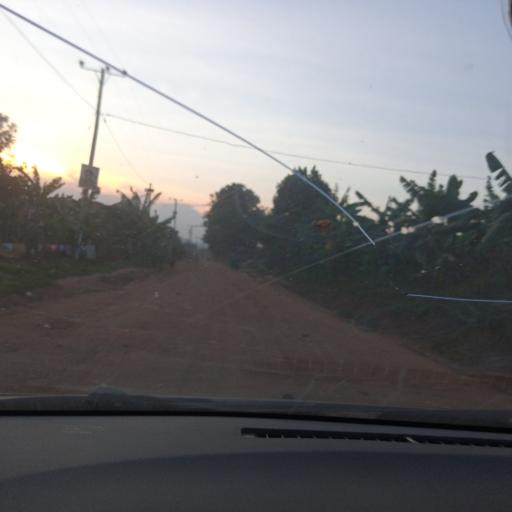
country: UG
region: Central Region
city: Masaka
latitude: -0.3117
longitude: 31.7659
